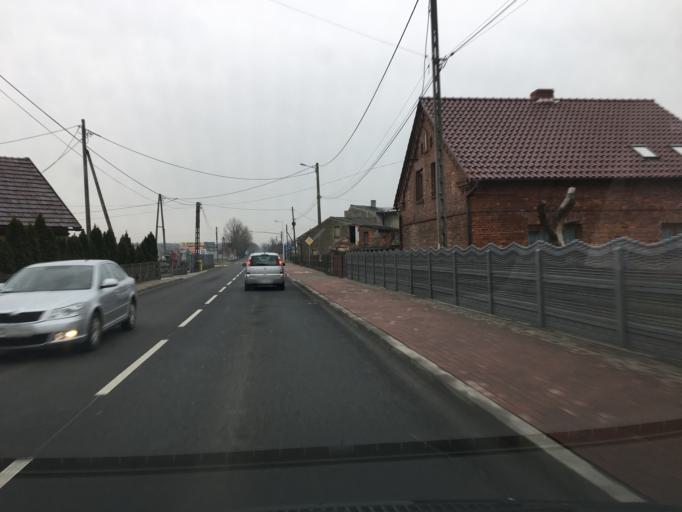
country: PL
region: Opole Voivodeship
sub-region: Powiat kedzierzynsko-kozielski
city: Kedzierzyn-Kozle
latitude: 50.3141
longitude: 18.2255
